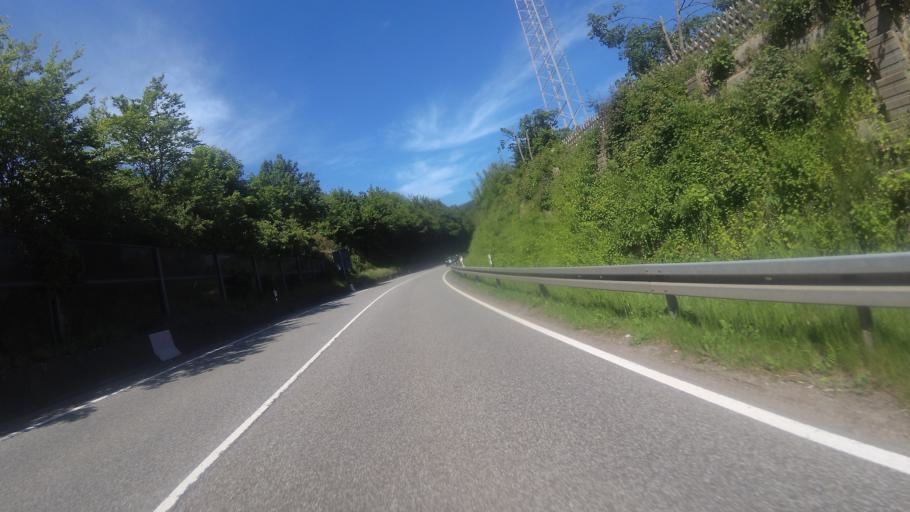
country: DE
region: Saarland
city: Quierschied
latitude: 49.3297
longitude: 7.0575
